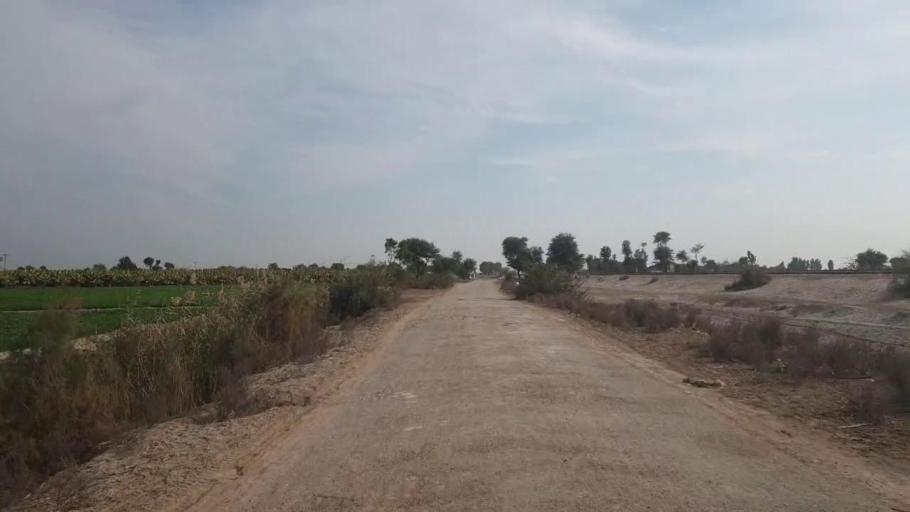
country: PK
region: Sindh
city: Shahpur Chakar
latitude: 26.0846
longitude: 68.4897
